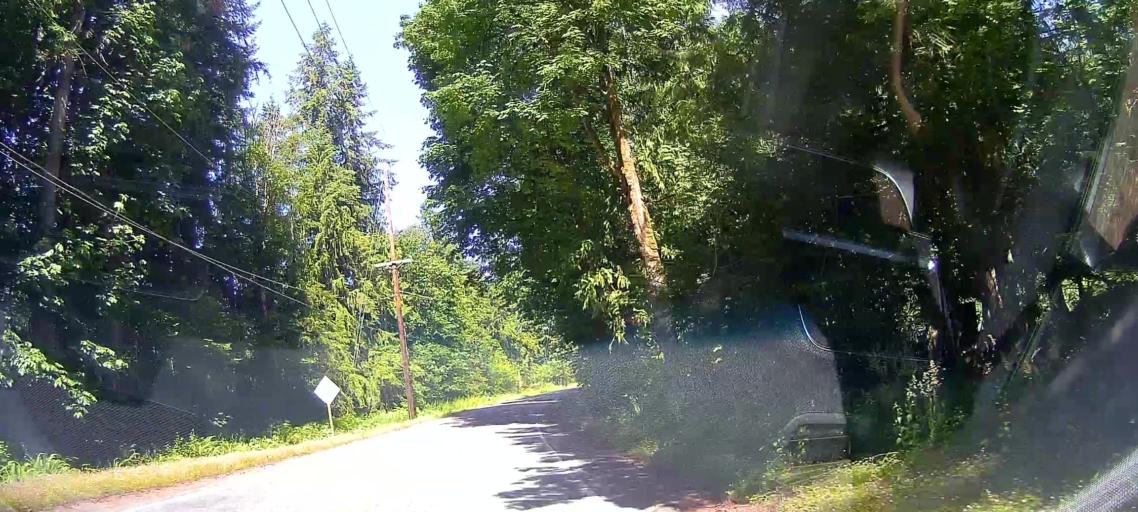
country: US
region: Washington
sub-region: Skagit County
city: Burlington
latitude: 48.5335
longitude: -122.3077
